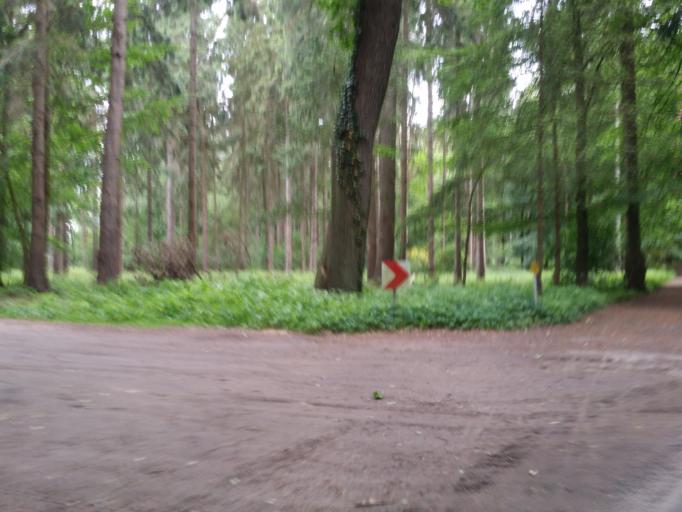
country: DE
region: Lower Saxony
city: Rastede
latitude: 53.2332
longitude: 8.2461
